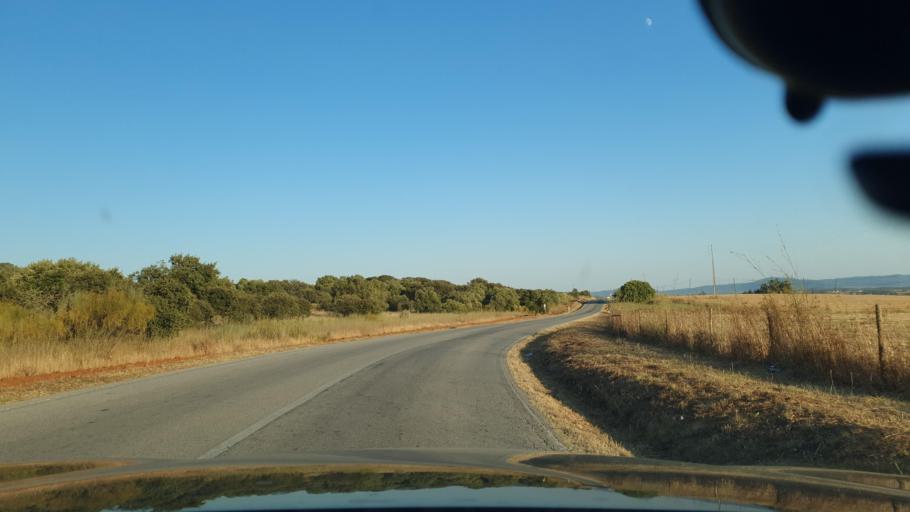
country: PT
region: Evora
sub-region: Estremoz
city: Estremoz
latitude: 38.8846
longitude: -7.6465
